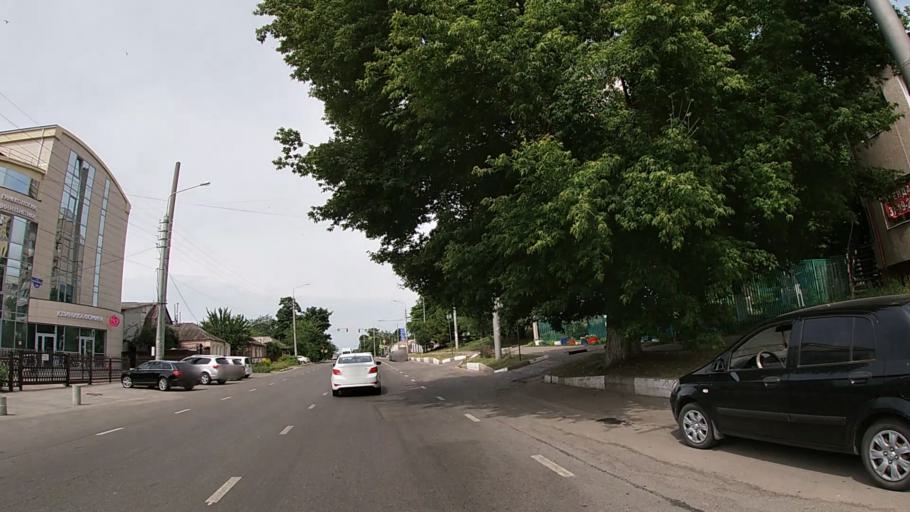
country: RU
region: Belgorod
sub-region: Belgorodskiy Rayon
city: Belgorod
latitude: 50.6006
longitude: 36.5756
